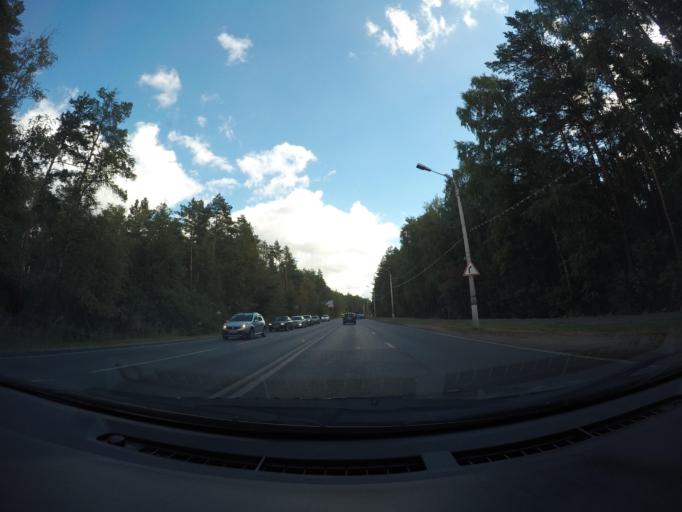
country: RU
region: Moskovskaya
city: Ramenskoye
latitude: 55.5849
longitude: 38.2277
